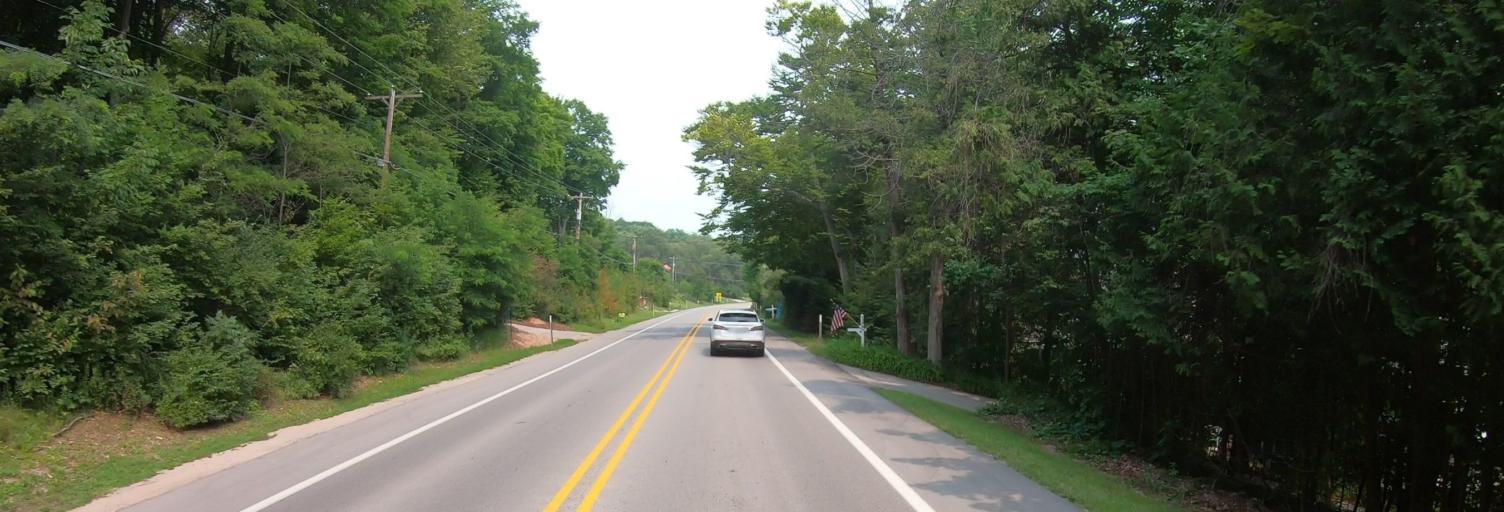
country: US
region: Michigan
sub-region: Leelanau County
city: Leland
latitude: 45.0001
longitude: -85.7717
